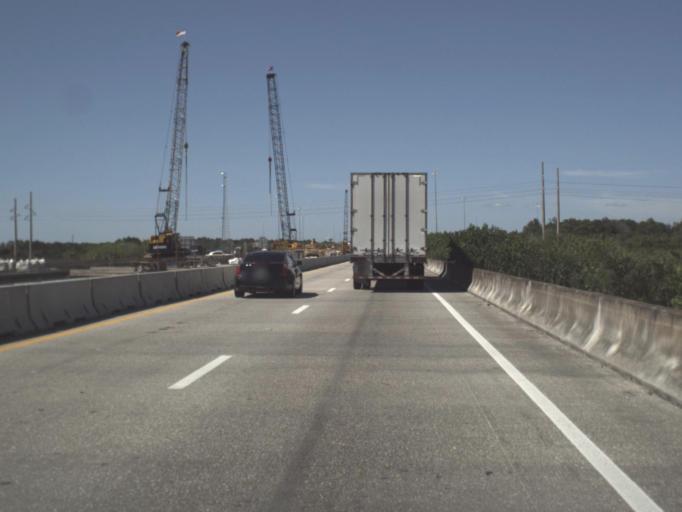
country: US
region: Florida
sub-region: Lee County
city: Tice
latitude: 26.7081
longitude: -81.8059
